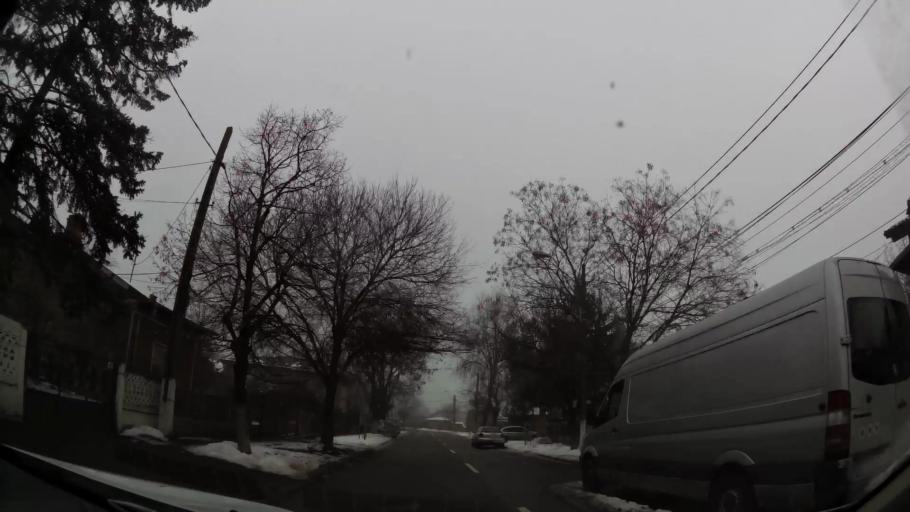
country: RO
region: Ilfov
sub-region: Comuna Chiajna
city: Rosu
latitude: 44.4709
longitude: 26.0013
